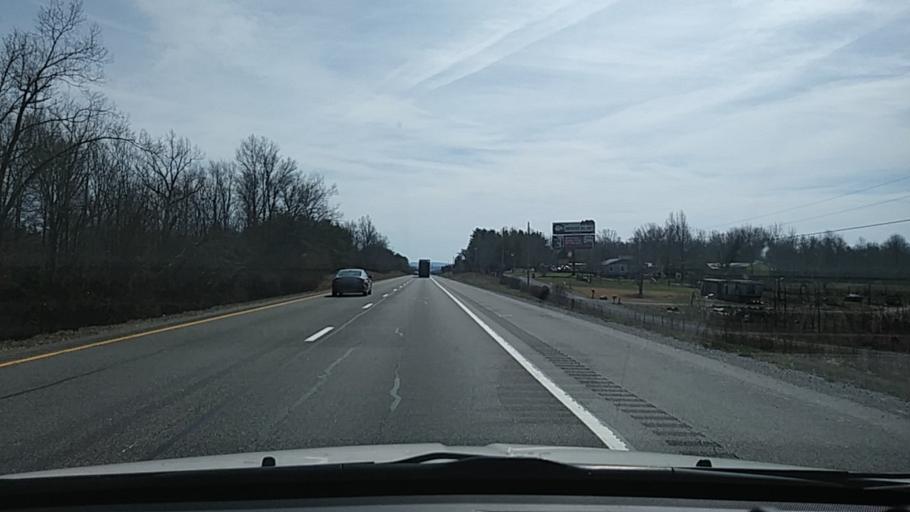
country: US
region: Tennessee
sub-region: Cumberland County
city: Crossville
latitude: 36.0251
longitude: -85.0857
